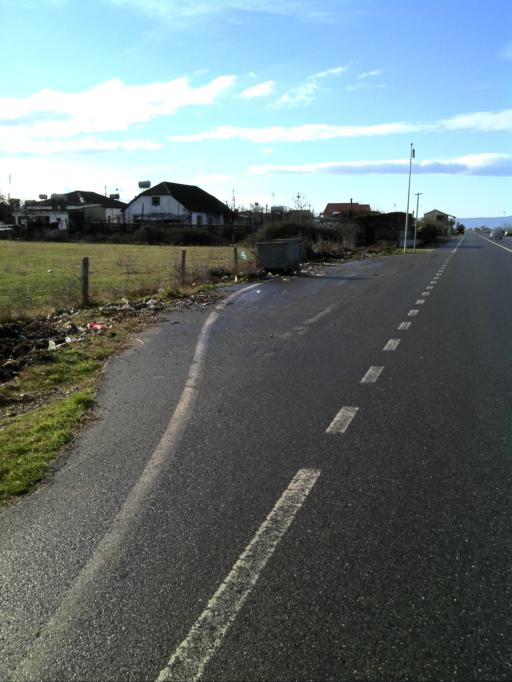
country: AL
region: Shkoder
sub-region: Rrethi i Malesia e Madhe
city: Koplik
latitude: 42.2580
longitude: 19.4279
